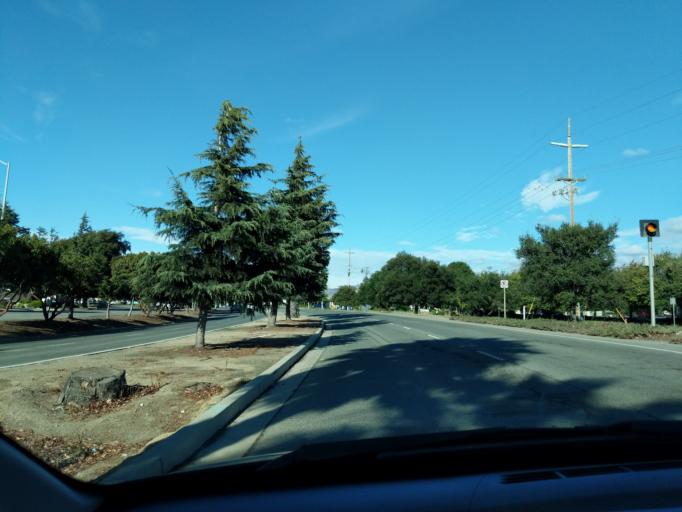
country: US
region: California
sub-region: Monterey County
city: Salinas
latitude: 36.6533
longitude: -121.6382
